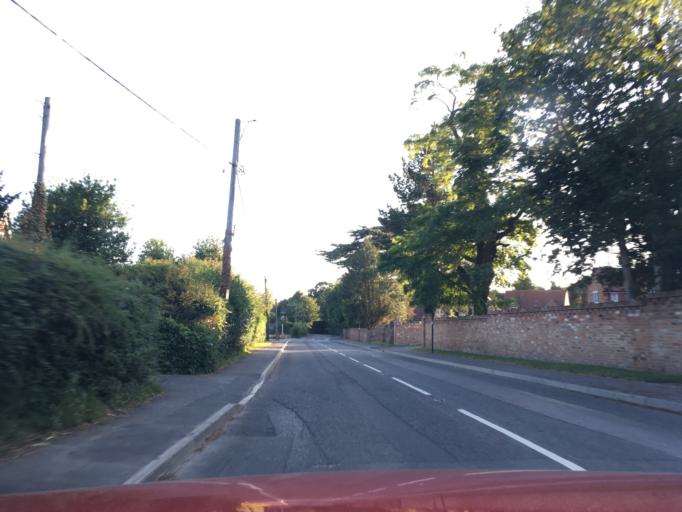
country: GB
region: England
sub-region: West Berkshire
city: Hermitage
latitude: 51.4533
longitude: -1.2753
